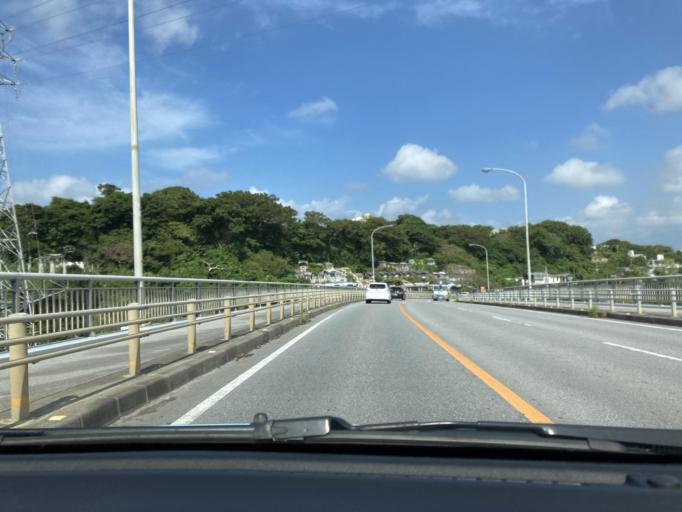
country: JP
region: Okinawa
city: Chatan
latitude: 26.2895
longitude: 127.7856
